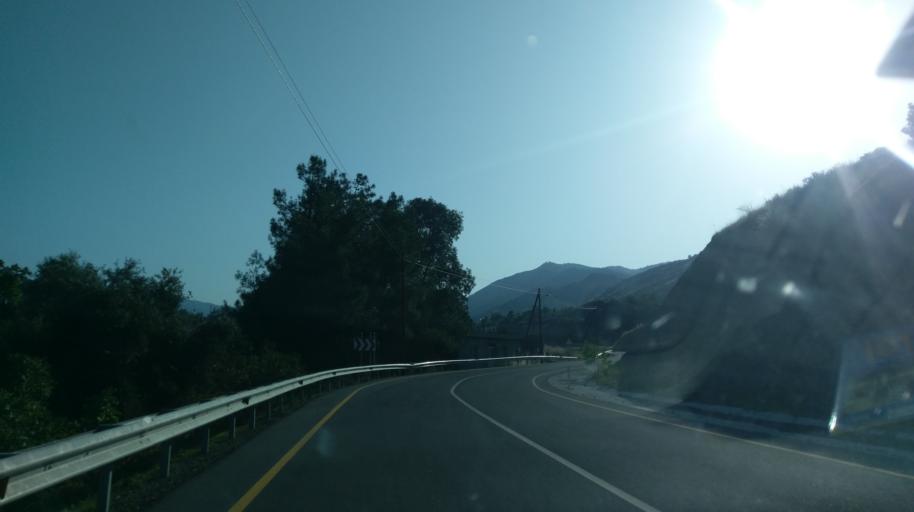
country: CY
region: Lefkosia
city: Lefka
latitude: 35.0873
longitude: 32.8422
